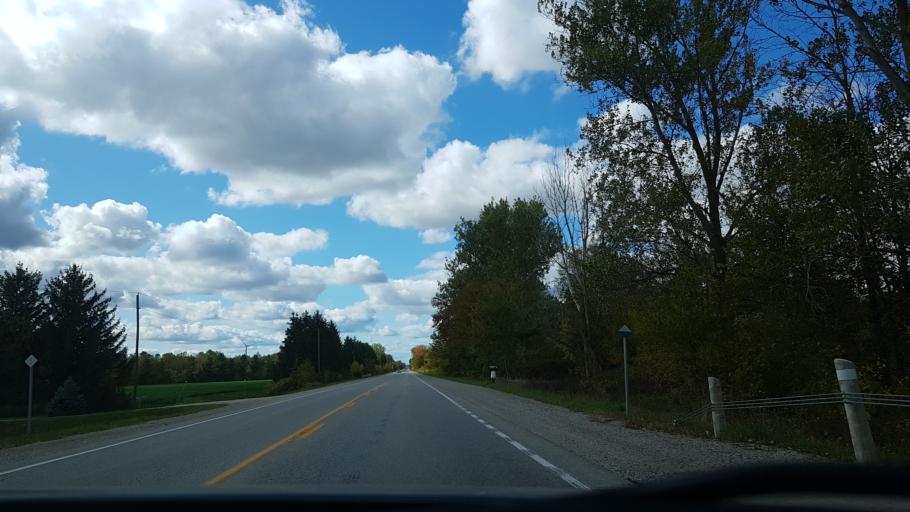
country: CA
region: Ontario
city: South Huron
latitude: 43.3554
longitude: -81.5445
